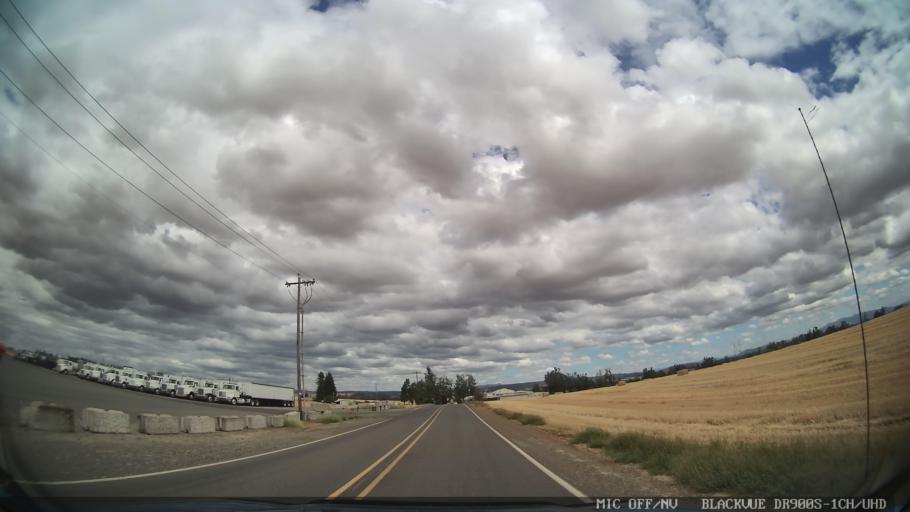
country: US
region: Oregon
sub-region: Marion County
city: Sublimity
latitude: 44.8675
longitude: -122.8066
